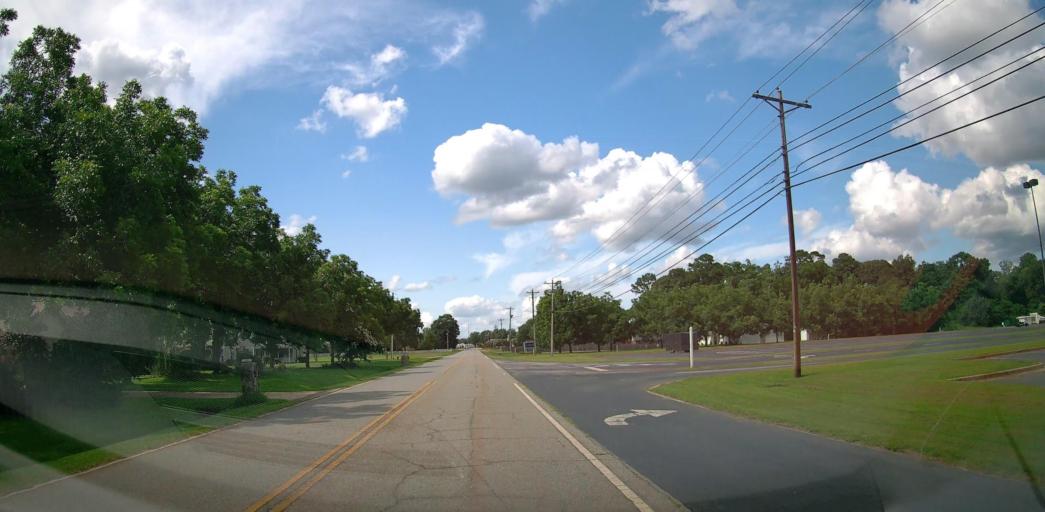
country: US
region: Georgia
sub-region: Houston County
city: Centerville
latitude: 32.5848
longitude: -83.6664
